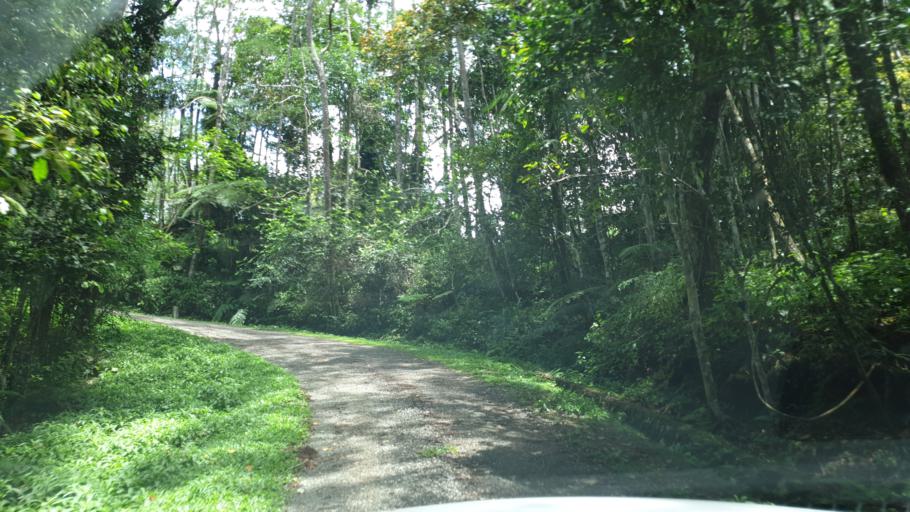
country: PG
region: National Capital
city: Port Moresby
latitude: -9.4354
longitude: 147.3648
